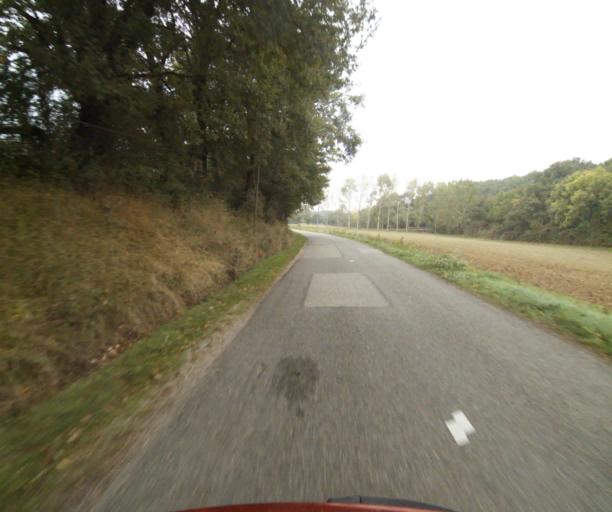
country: FR
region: Midi-Pyrenees
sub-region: Departement du Tarn-et-Garonne
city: Verdun-sur-Garonne
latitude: 43.8323
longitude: 1.1921
